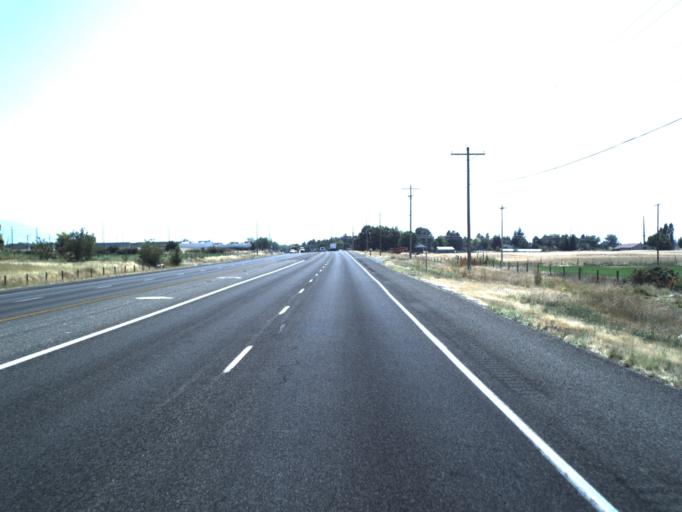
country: US
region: Utah
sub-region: Cache County
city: Smithfield
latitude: 41.8579
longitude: -111.8311
